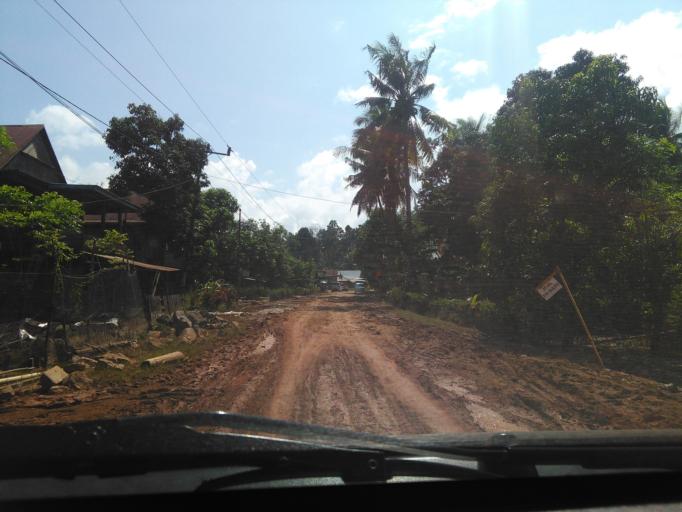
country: ID
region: South Sulawesi
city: Tancung
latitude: -4.0160
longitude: 119.9248
